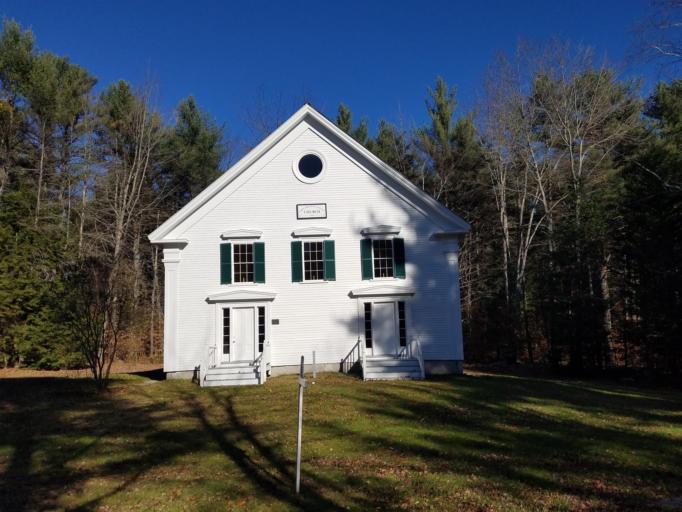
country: US
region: New Hampshire
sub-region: Carroll County
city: Effingham
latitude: 43.6785
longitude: -71.0269
